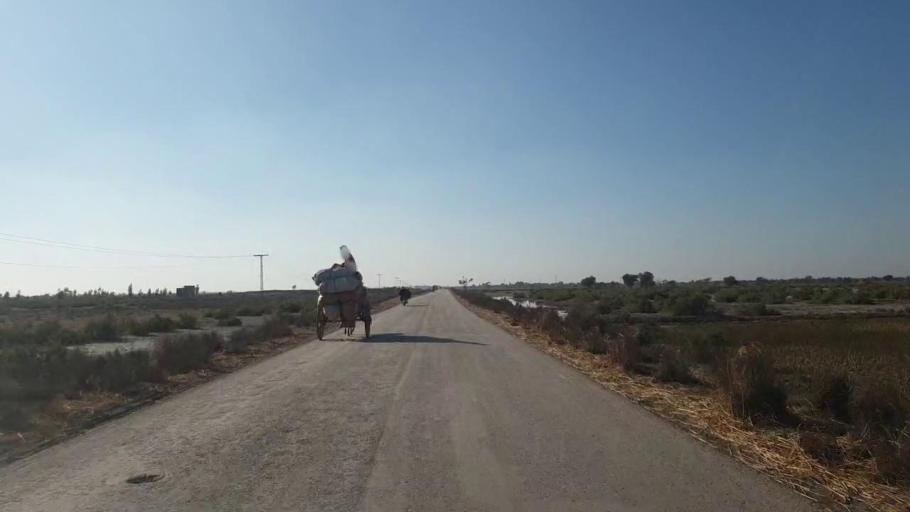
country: PK
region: Sindh
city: New Badah
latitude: 27.3249
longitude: 68.0577
